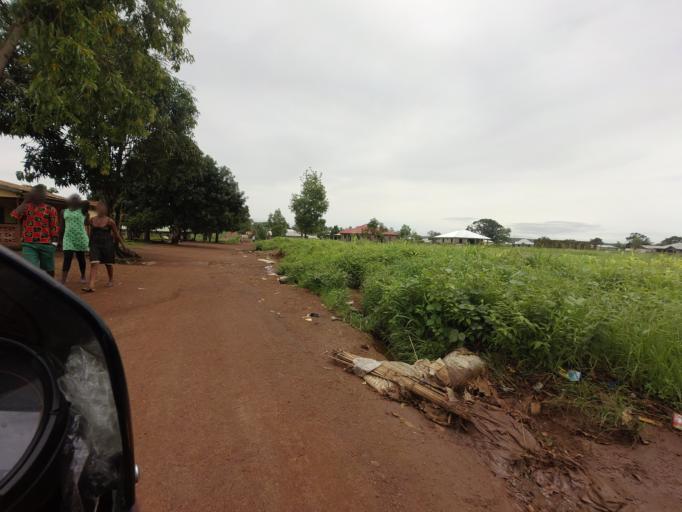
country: SL
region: Northern Province
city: Kambia
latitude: 9.1091
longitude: -12.9298
